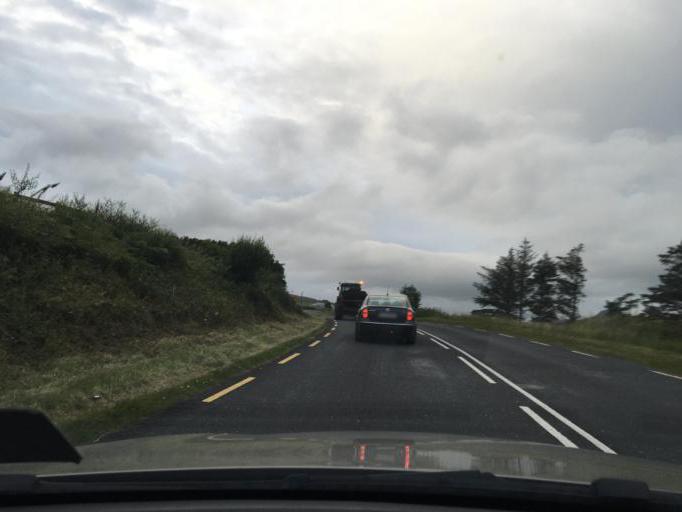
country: IE
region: Ulster
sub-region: County Donegal
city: Buncrana
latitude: 55.1806
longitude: -7.4066
